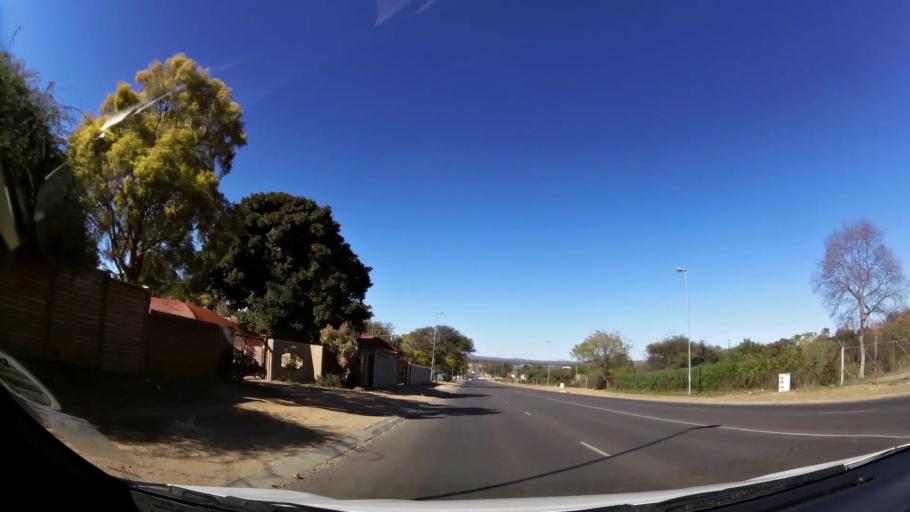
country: ZA
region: Limpopo
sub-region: Capricorn District Municipality
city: Polokwane
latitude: -23.9112
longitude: 29.4747
